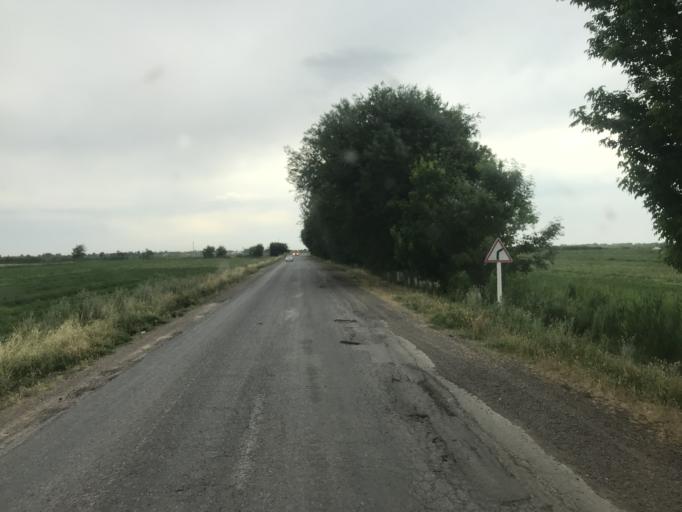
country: KZ
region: Ongtustik Qazaqstan
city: Asykata
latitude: 40.9513
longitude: 68.4479
